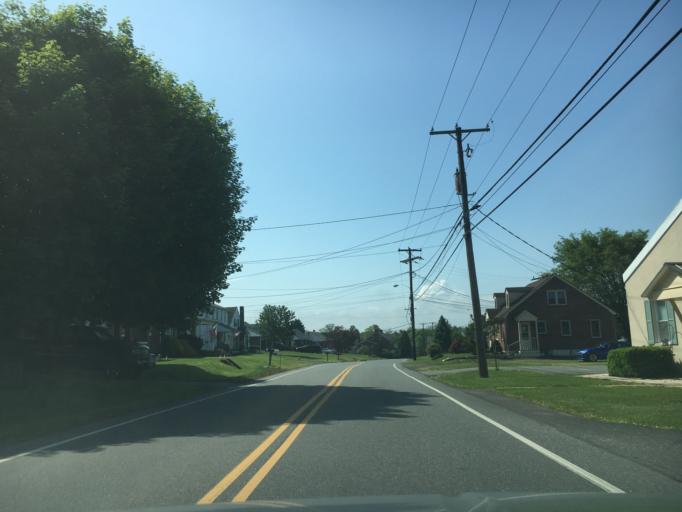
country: US
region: Pennsylvania
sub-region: Berks County
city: Boyertown
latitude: 40.3351
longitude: -75.6240
